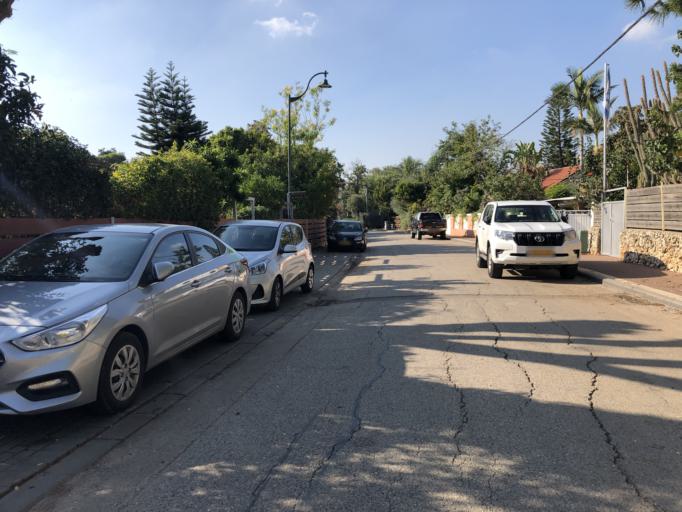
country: IL
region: Central District
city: Jaljulya
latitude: 32.1329
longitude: 34.9257
